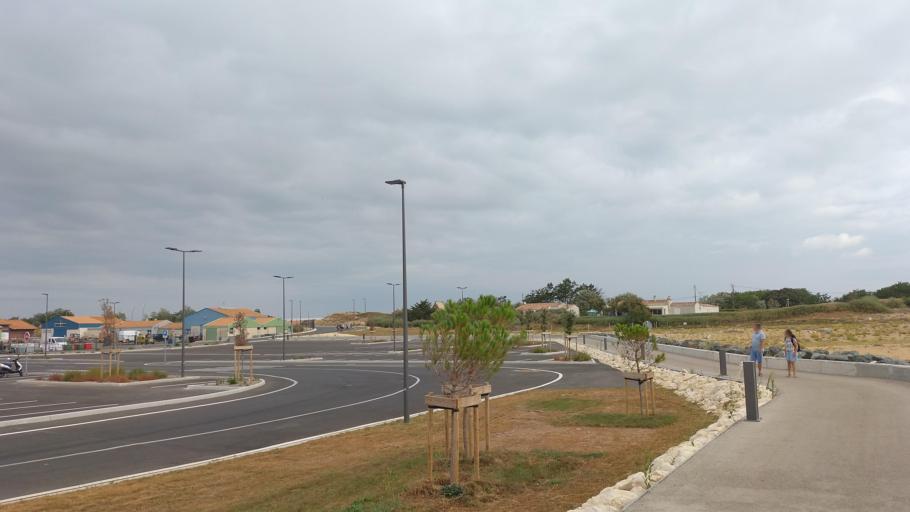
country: FR
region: Poitou-Charentes
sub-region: Departement de la Charente-Maritime
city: Dolus-d'Oleron
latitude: 45.9121
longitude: -1.3236
